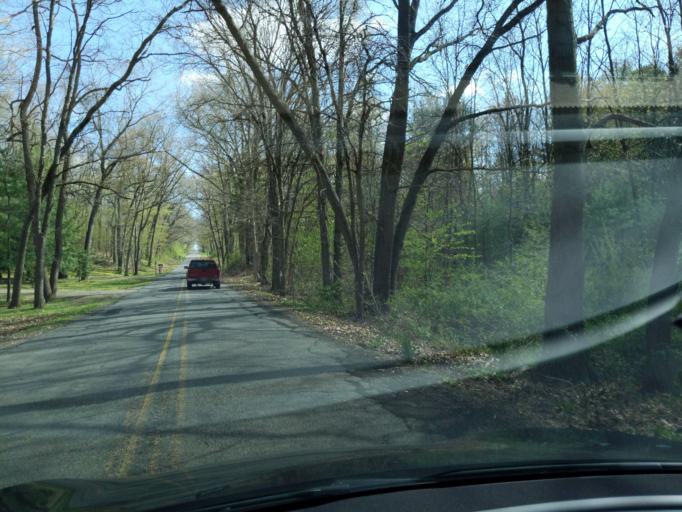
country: US
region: Michigan
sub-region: Ingham County
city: Leslie
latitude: 42.3607
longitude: -84.5318
